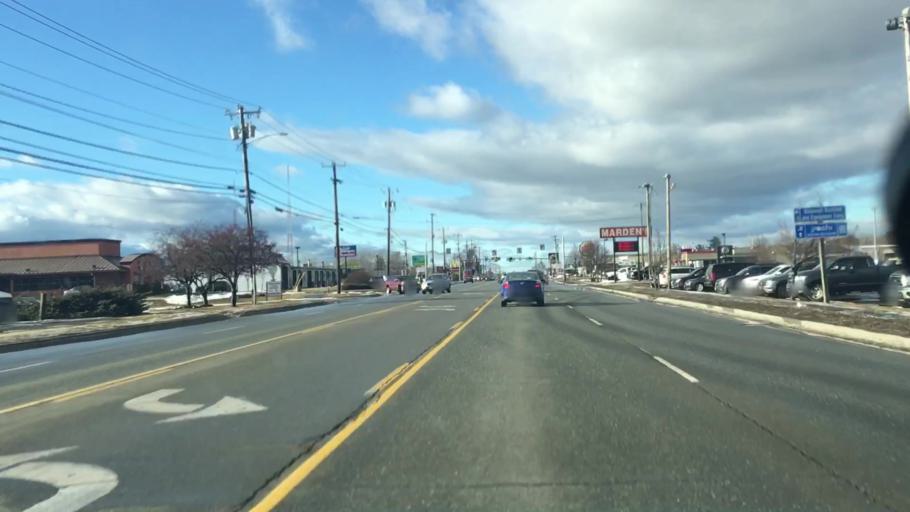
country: US
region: Maine
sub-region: Penobscot County
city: Brewer
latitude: 44.7794
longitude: -68.7401
